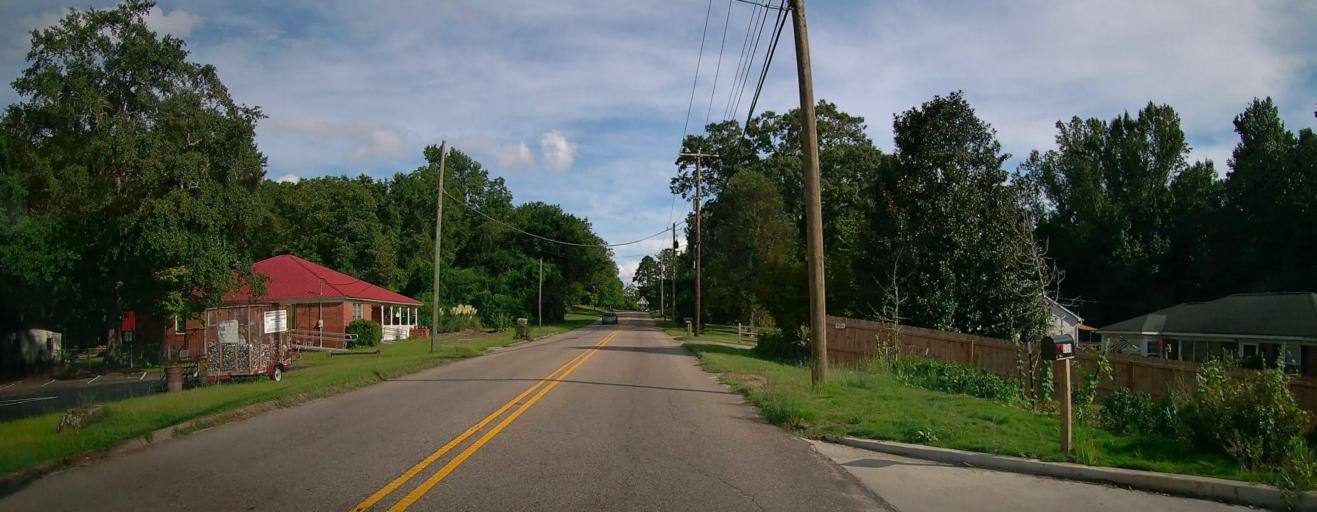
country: US
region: Alabama
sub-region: Russell County
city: Phenix City
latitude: 32.4952
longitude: -85.0138
